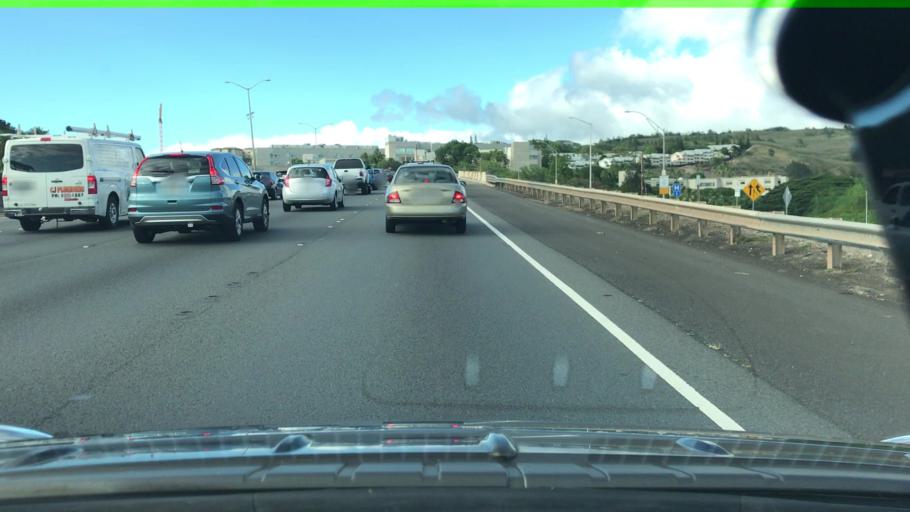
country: US
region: Hawaii
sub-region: Honolulu County
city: Halawa Heights
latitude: 21.3592
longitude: -157.8994
